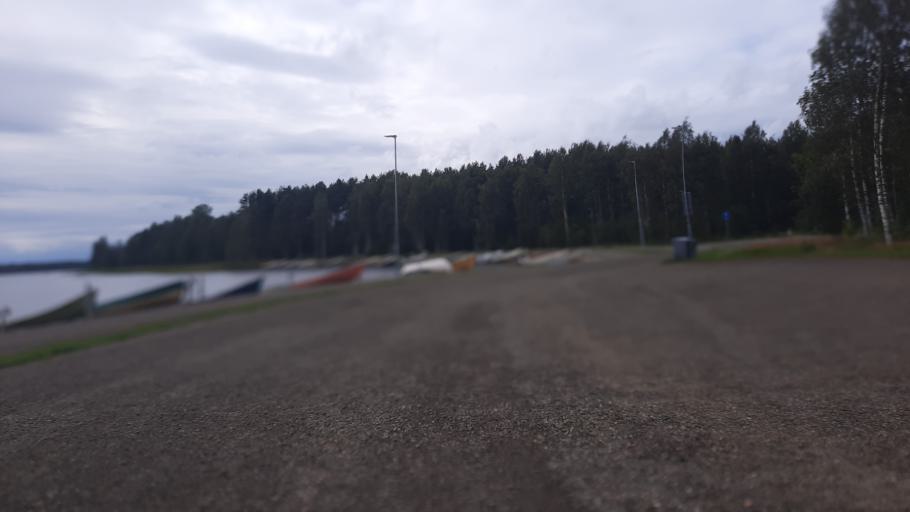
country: FI
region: North Karelia
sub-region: Joensuu
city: Joensuu
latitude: 62.6121
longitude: 29.8468
